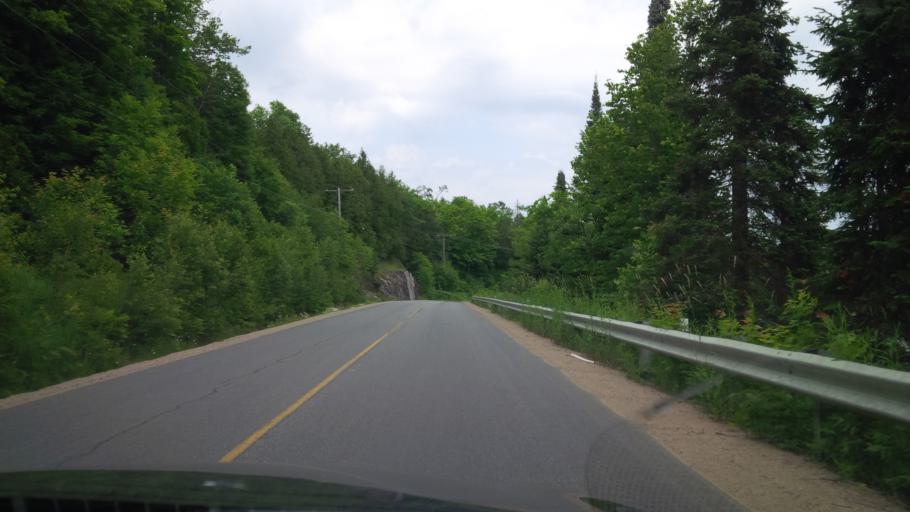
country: CA
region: Ontario
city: Huntsville
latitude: 45.5842
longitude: -79.2169
